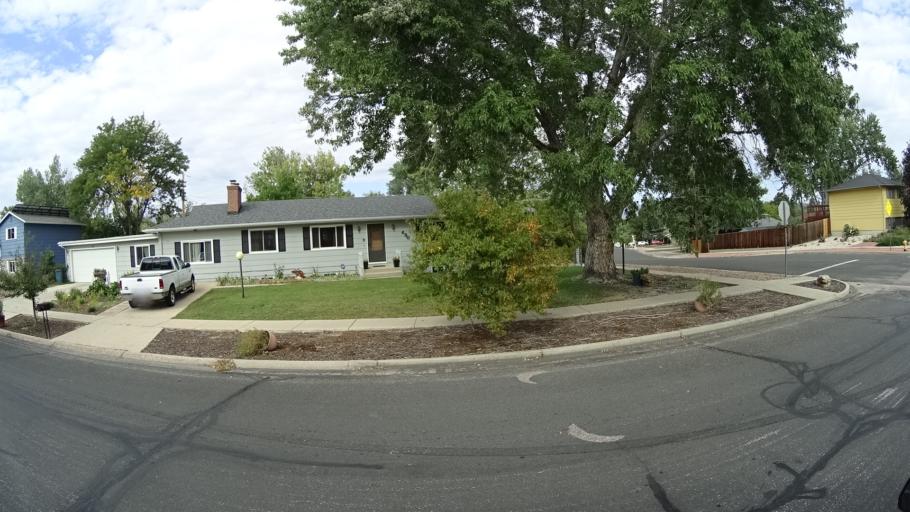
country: US
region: Colorado
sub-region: El Paso County
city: Cimarron Hills
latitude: 38.8434
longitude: -104.7502
